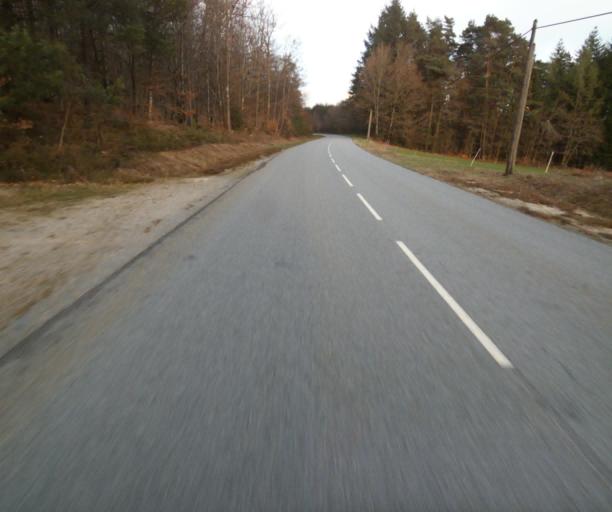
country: FR
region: Limousin
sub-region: Departement de la Correze
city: Correze
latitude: 45.2799
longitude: 1.9361
